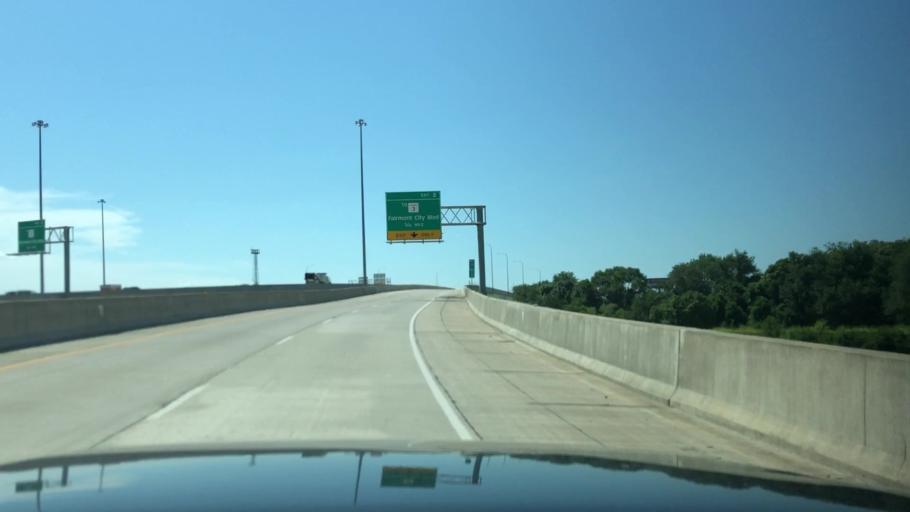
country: US
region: Illinois
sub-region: Saint Clair County
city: East Saint Louis
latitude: 38.6343
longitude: -90.1439
